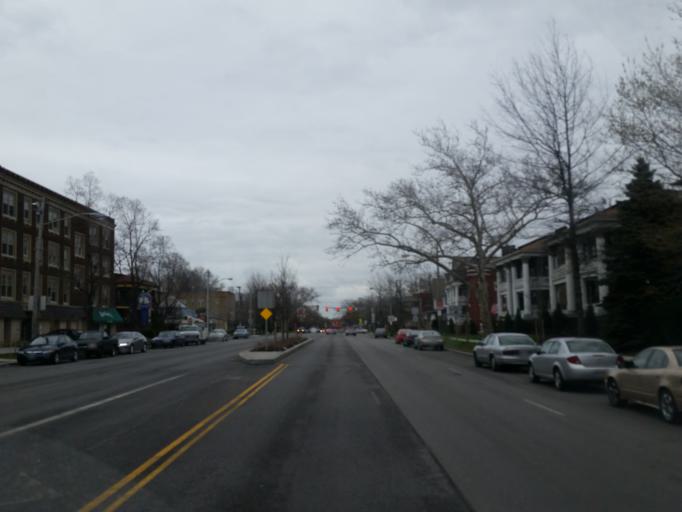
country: US
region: Ohio
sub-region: Cuyahoga County
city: Lakewood
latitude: 41.4864
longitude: -81.7633
